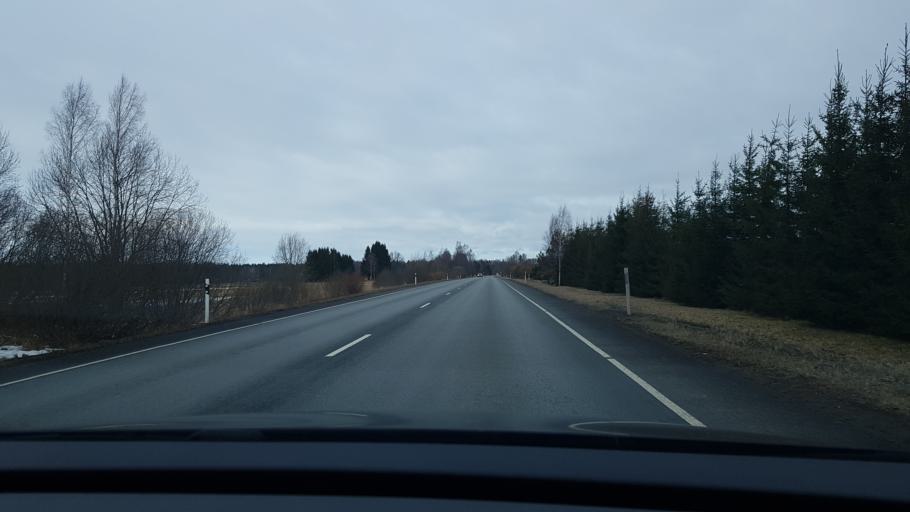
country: EE
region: Paernumaa
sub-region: Paikuse vald
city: Paikuse
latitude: 58.2296
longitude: 24.7000
